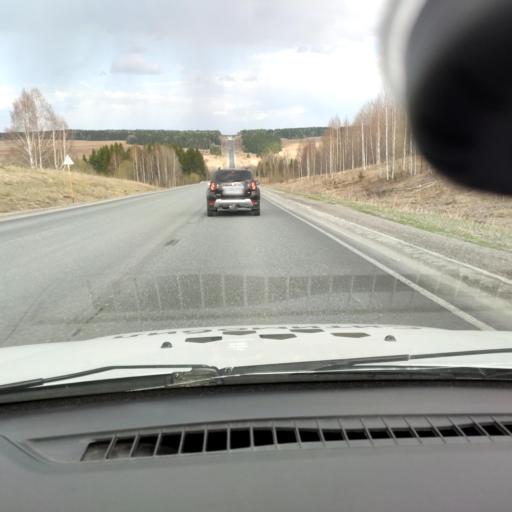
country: RU
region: Perm
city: Verkhnechusovskiye Gorodki
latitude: 58.2120
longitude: 57.1314
